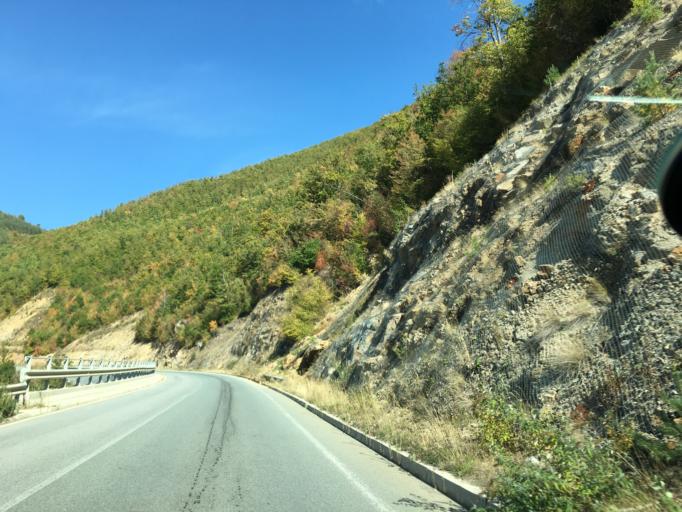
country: BG
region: Smolyan
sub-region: Obshtina Devin
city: Devin
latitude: 41.7487
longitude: 24.4370
